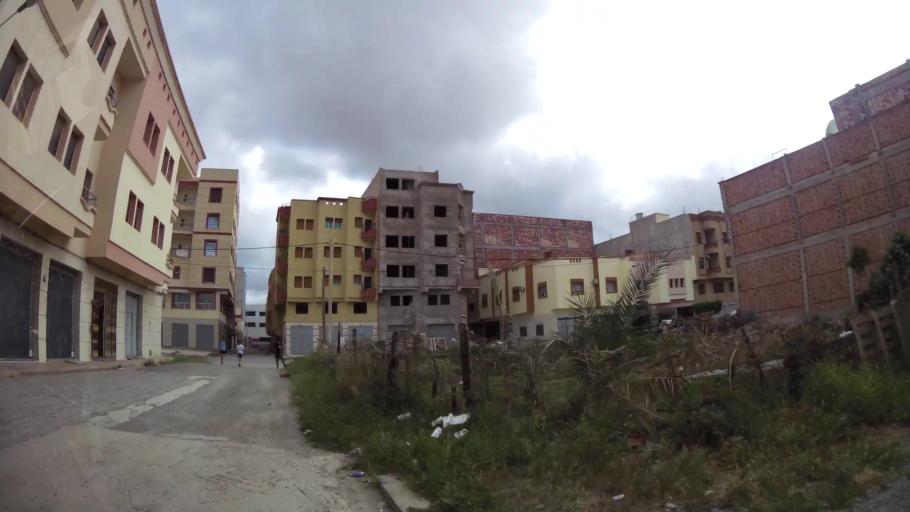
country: MA
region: Oriental
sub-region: Nador
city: Nador
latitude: 35.1595
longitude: -2.9331
